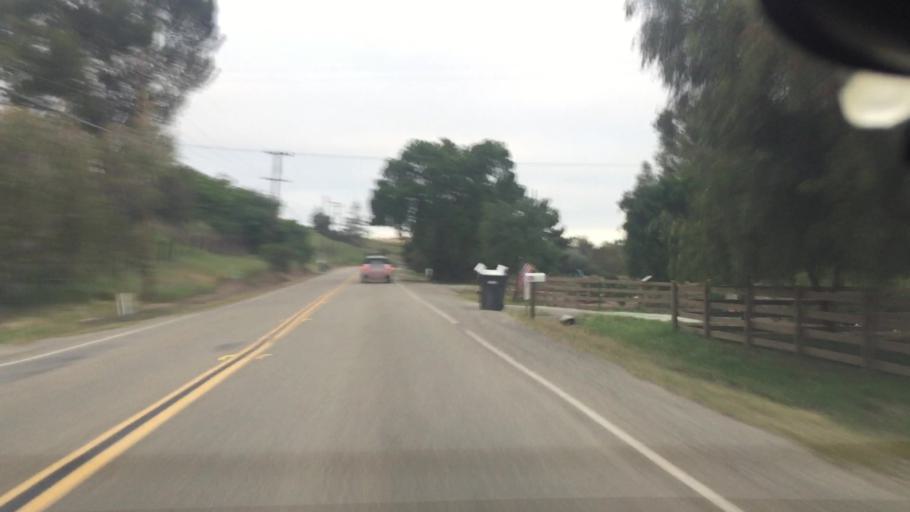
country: US
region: California
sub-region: Alameda County
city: Livermore
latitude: 37.6516
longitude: -121.6658
